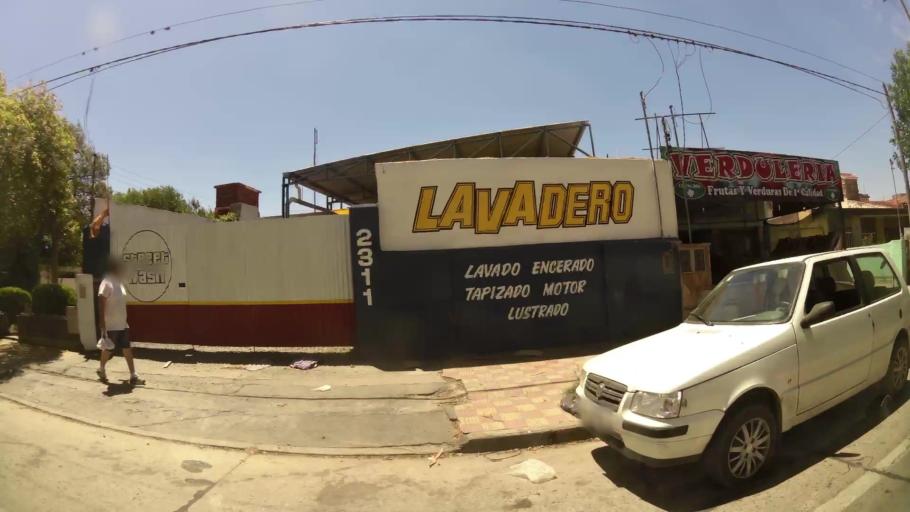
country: AR
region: Cordoba
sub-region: Departamento de Capital
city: Cordoba
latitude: -31.3786
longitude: -64.1397
